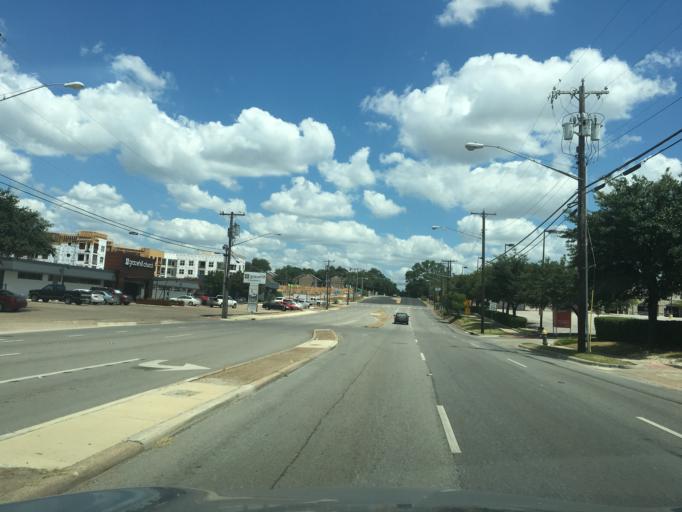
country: US
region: Texas
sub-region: Dallas County
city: Richardson
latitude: 32.8645
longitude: -96.7106
